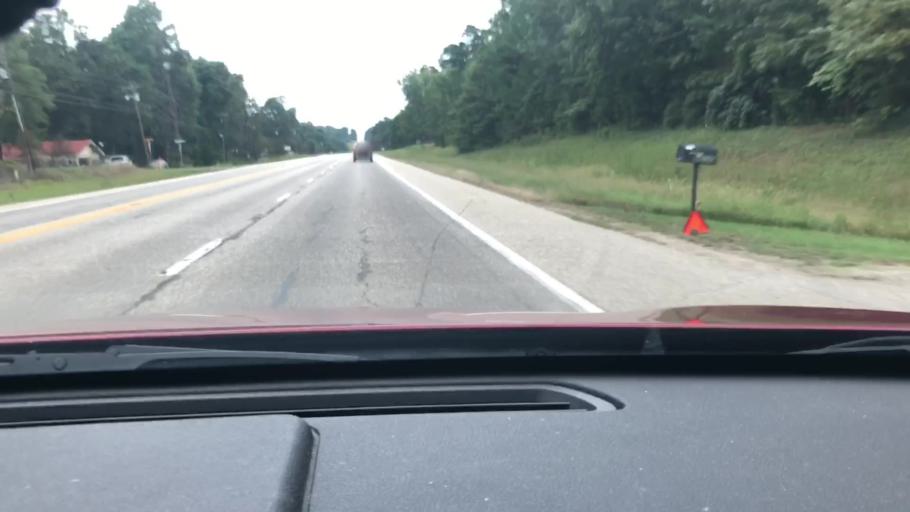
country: US
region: Arkansas
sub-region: Miller County
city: Texarkana
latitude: 33.4296
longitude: -93.9553
